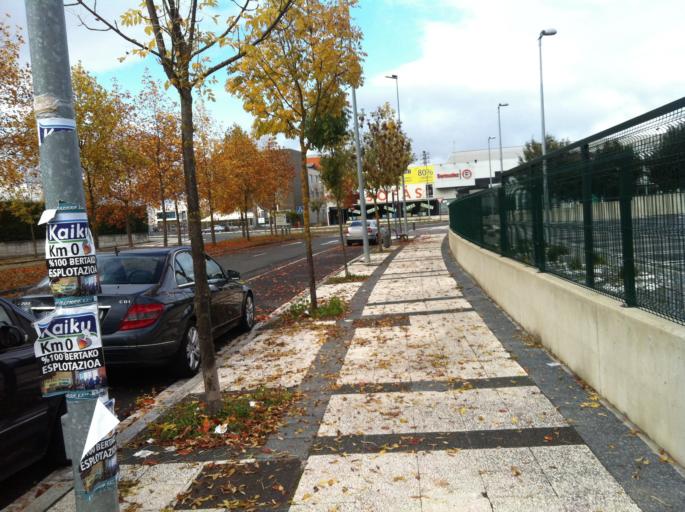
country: ES
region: Basque Country
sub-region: Provincia de Alava
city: Gasteiz / Vitoria
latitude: 42.8553
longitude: -2.7110
